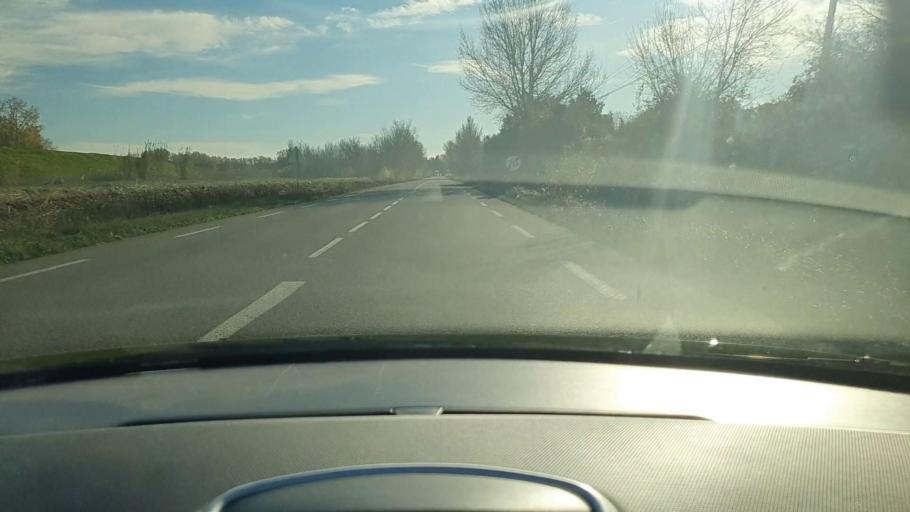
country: FR
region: Languedoc-Roussillon
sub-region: Departement du Gard
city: Fourques
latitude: 43.7174
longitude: 4.6062
